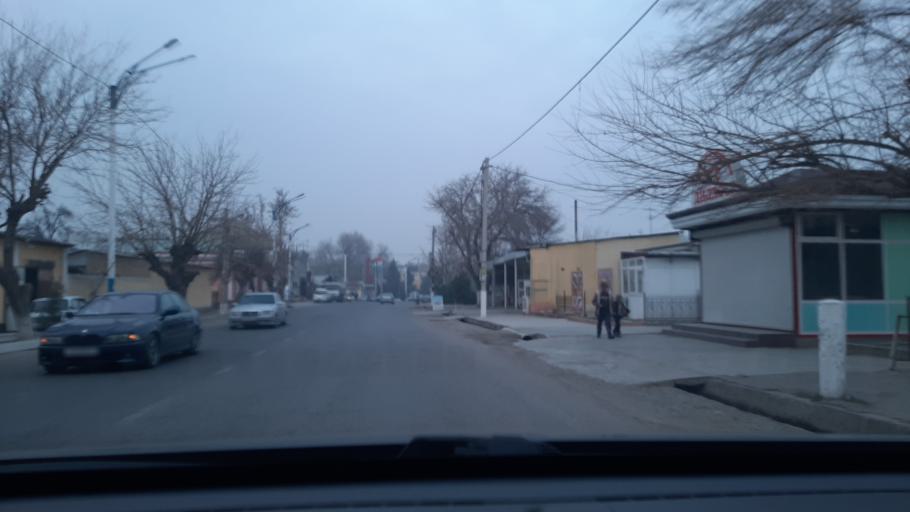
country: TJ
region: Viloyati Sughd
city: Khujand
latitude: 40.2676
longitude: 69.6015
